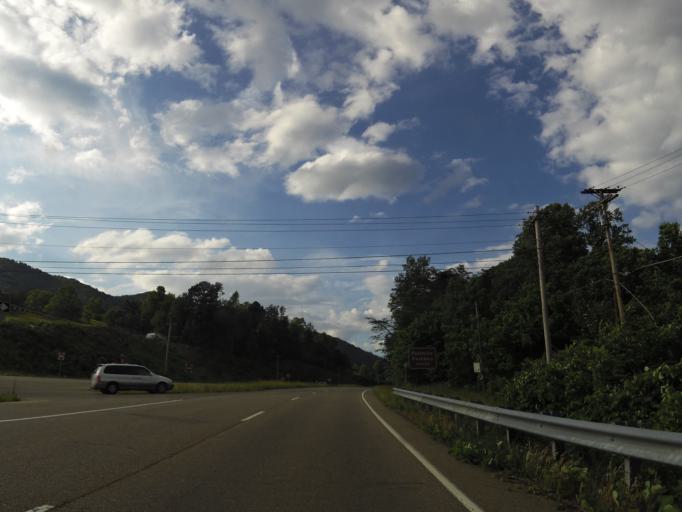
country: US
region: Tennessee
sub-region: Blount County
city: Wildwood
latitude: 35.7146
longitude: -83.8204
